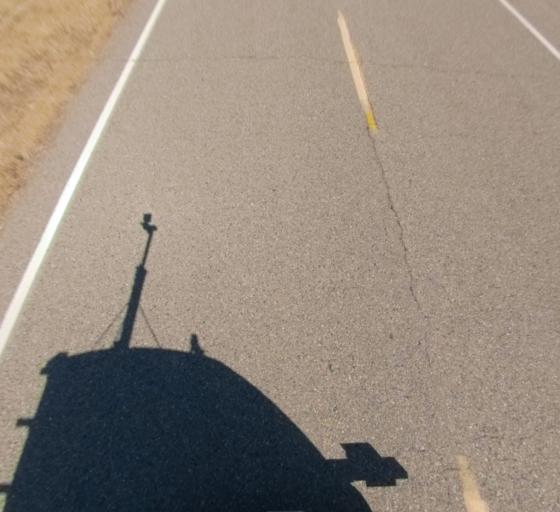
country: US
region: California
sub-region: Fresno County
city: Biola
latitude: 36.8494
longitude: -119.9451
